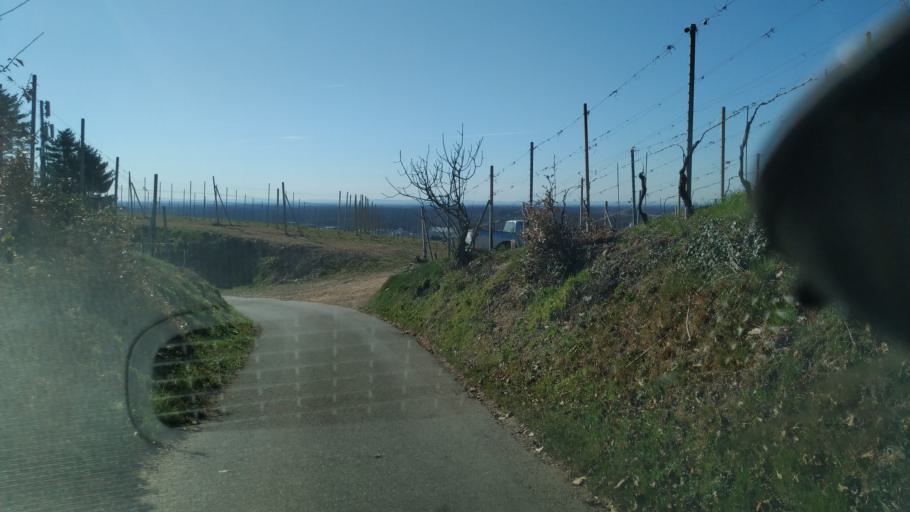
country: IT
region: Piedmont
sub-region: Provincia di Vercelli
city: Gattinara
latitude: 45.6228
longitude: 8.3656
